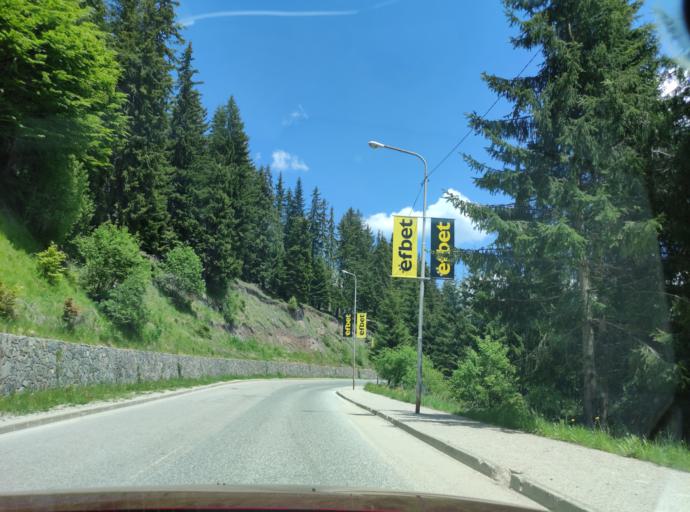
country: BG
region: Smolyan
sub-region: Obshtina Smolyan
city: Smolyan
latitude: 41.6428
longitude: 24.6924
